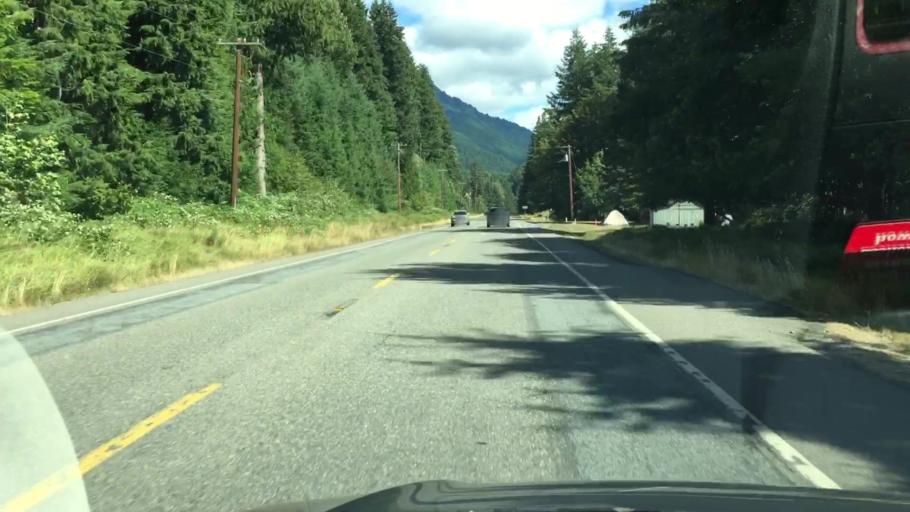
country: US
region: Washington
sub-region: Pierce County
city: Eatonville
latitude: 46.7572
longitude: -121.9912
